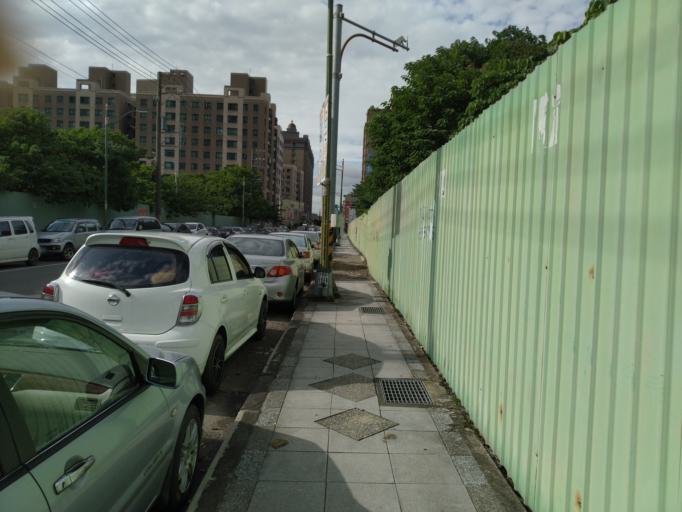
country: TW
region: Taiwan
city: Taoyuan City
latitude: 24.9763
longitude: 121.2526
